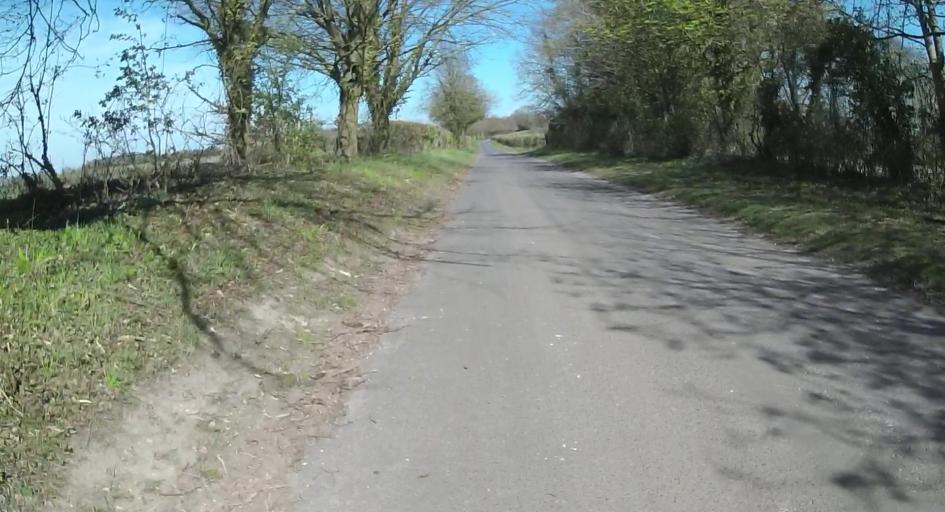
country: GB
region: England
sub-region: Hampshire
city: Old Basing
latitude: 51.2379
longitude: -0.9972
